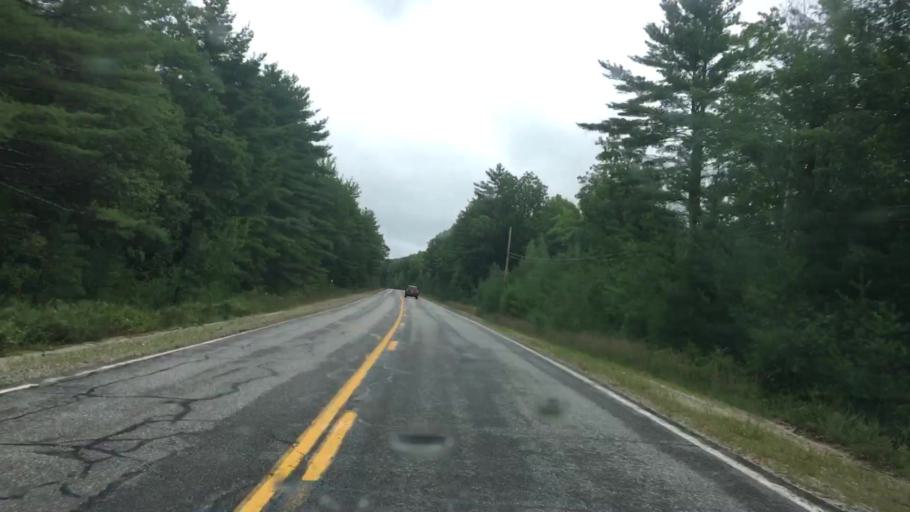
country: US
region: Maine
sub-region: Oxford County
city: Brownfield
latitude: 43.9757
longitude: -70.9250
